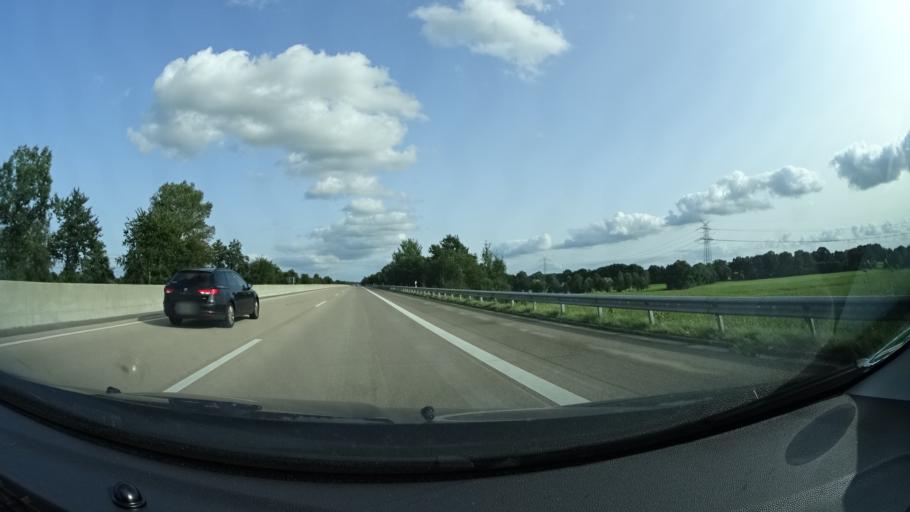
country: DE
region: Schleswig-Holstein
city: Horst
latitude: 53.8214
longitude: 9.6475
